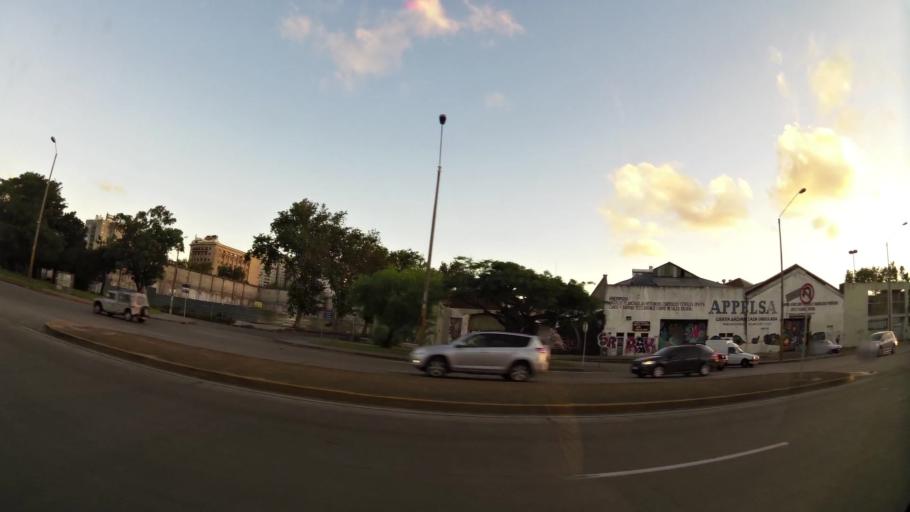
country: UY
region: Montevideo
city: Montevideo
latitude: -34.8994
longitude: -56.1959
